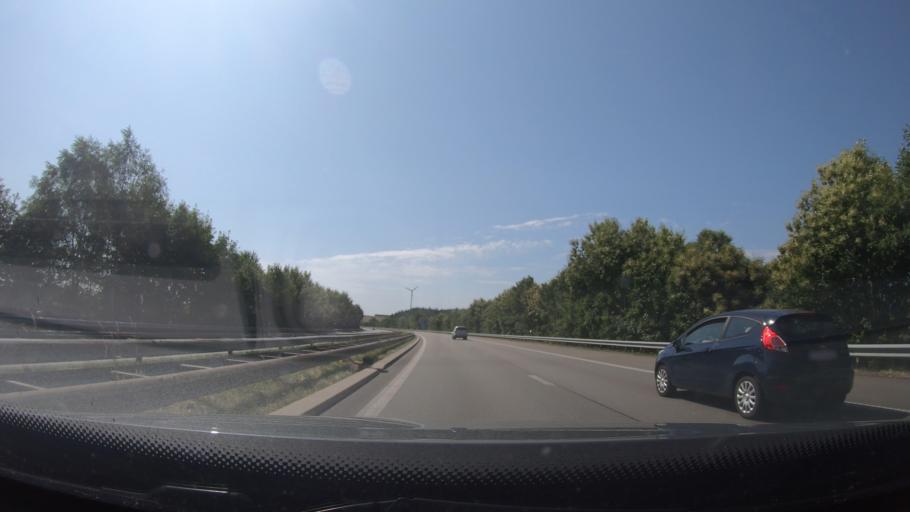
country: BE
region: Wallonia
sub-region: Province de Liege
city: Saint-Vith
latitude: 50.3003
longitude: 6.0804
